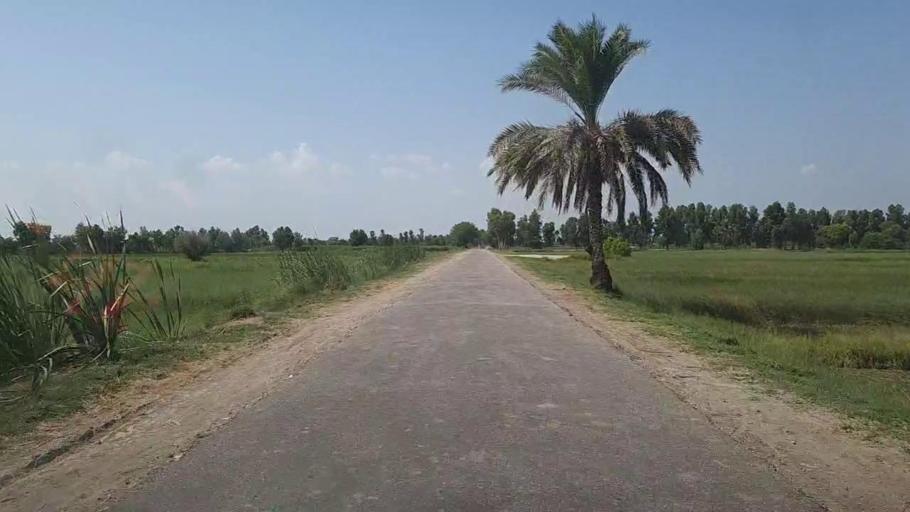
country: PK
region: Sindh
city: Khairpur
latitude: 28.0806
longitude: 69.6364
